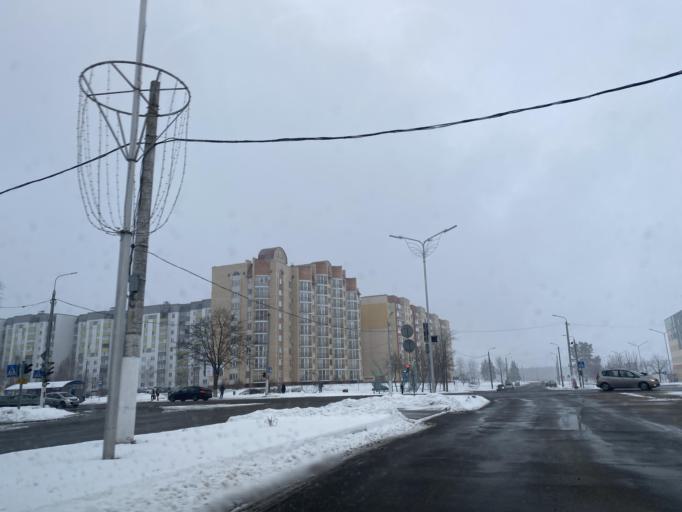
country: BY
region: Minsk
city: Horad Zhodzina
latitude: 54.0974
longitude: 28.3013
